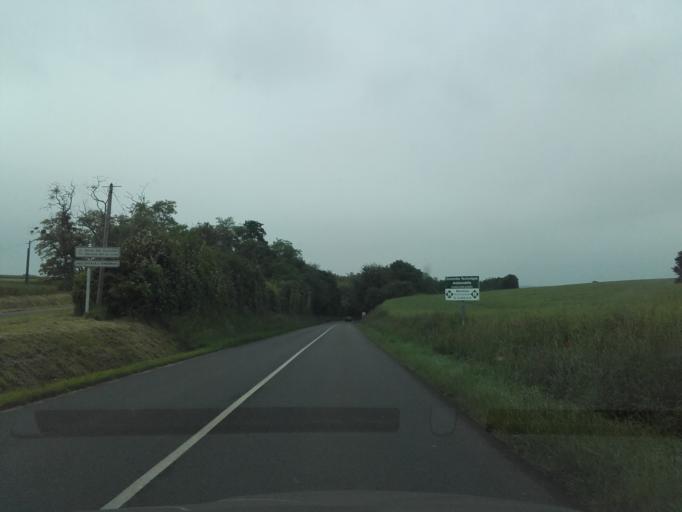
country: FR
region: Centre
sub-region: Departement du Loir-et-Cher
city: Montoire-sur-le-Loir
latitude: 47.7434
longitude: 0.8499
